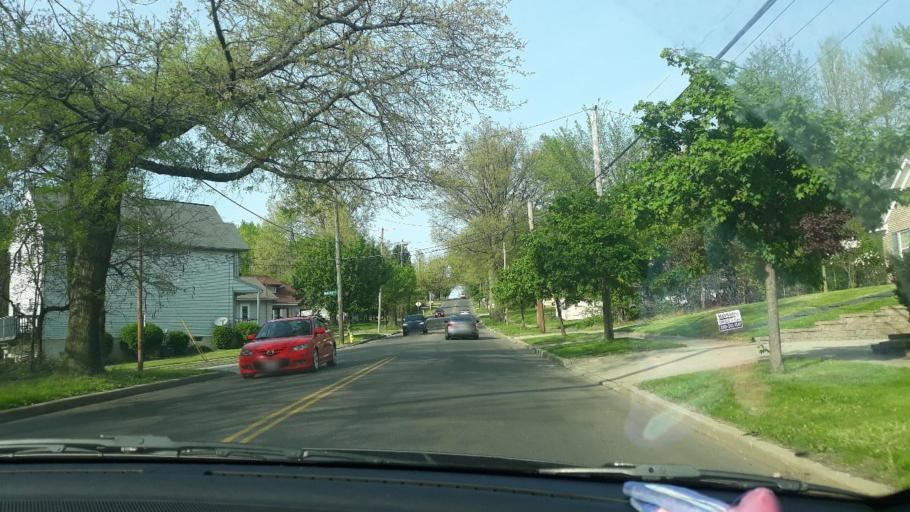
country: US
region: Ohio
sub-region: Summit County
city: Akron
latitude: 41.0760
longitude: -81.4791
